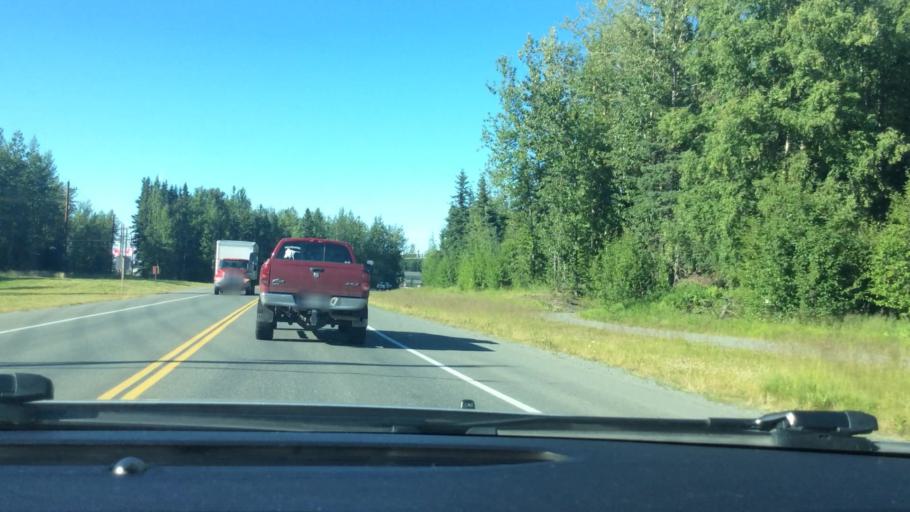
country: US
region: Alaska
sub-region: Anchorage Municipality
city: Elmendorf Air Force Base
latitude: 61.2429
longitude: -149.7055
